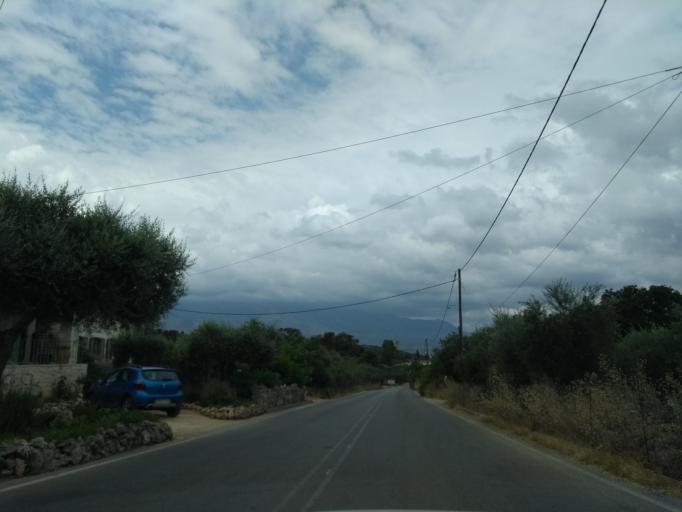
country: GR
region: Crete
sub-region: Nomos Chanias
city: Kalivai
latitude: 35.4077
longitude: 24.2053
